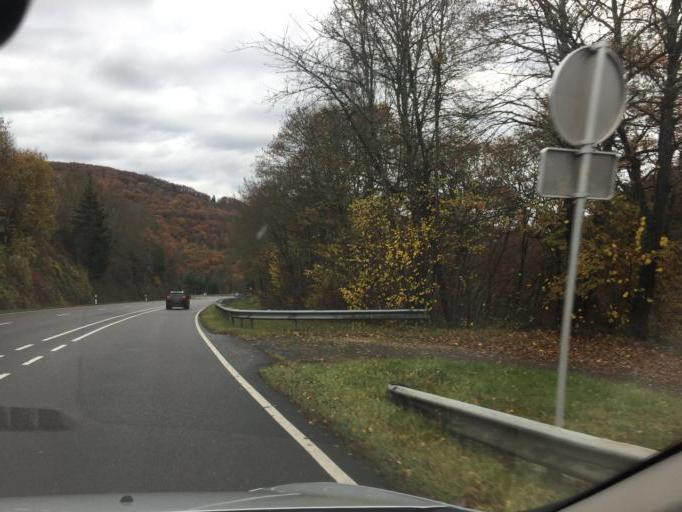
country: LU
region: Diekirch
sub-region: Canton de Wiltz
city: Goesdorf
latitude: 49.9024
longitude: 5.9592
